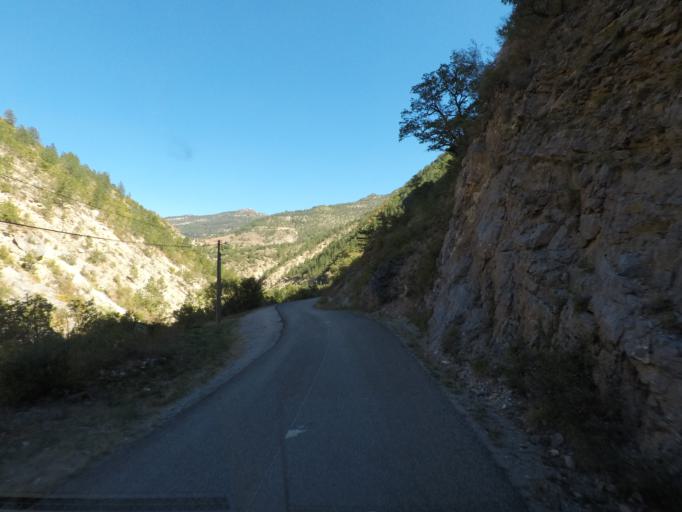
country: FR
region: Rhone-Alpes
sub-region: Departement de la Drome
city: Die
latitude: 44.6407
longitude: 5.2918
